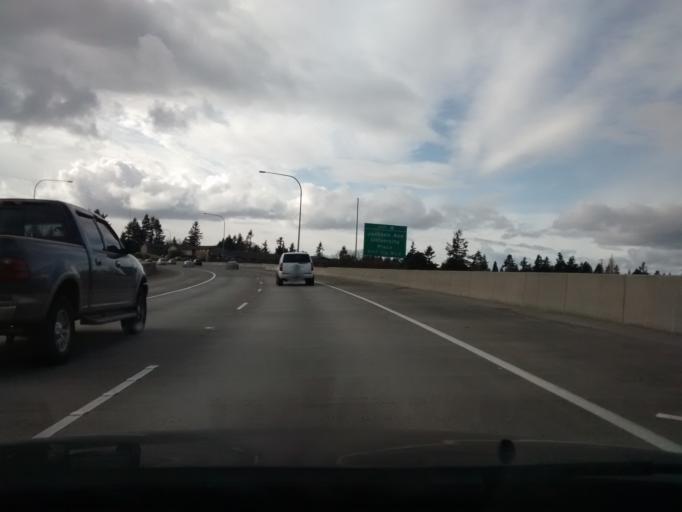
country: US
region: Washington
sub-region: Pierce County
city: Fircrest
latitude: 47.2573
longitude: -122.5156
